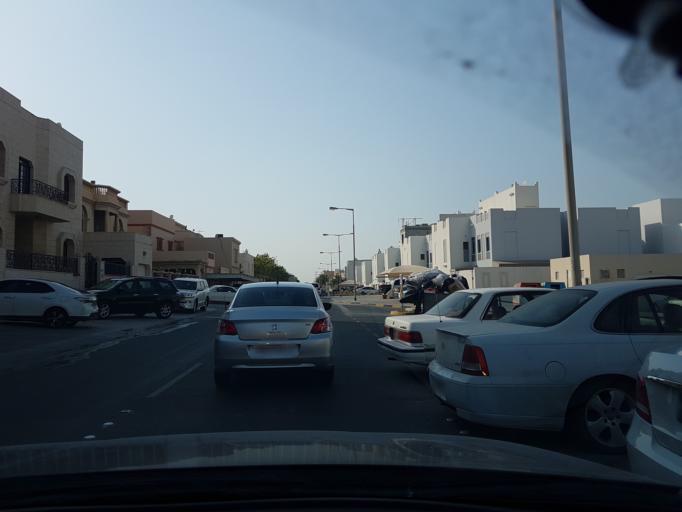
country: BH
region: Northern
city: Ar Rifa'
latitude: 26.1307
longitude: 50.5805
